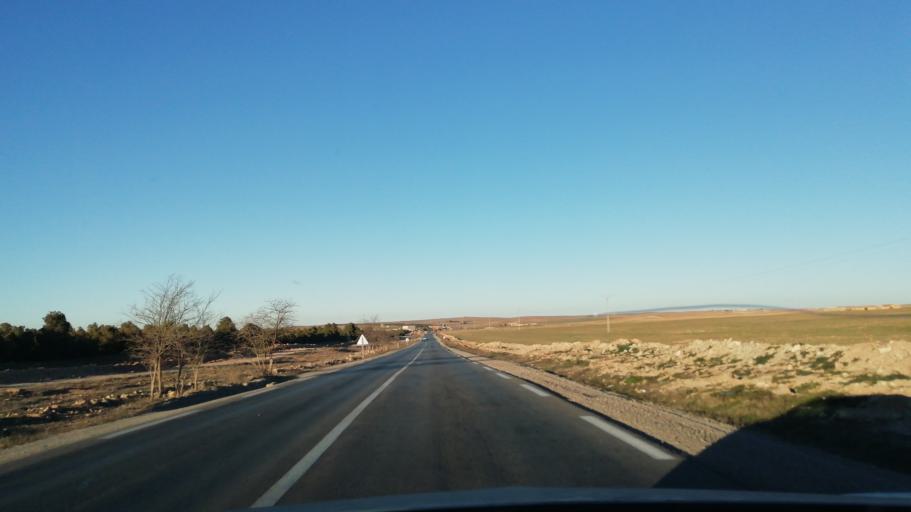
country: DZ
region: Saida
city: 'Ain el Hadjar
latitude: 34.5631
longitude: 0.1201
